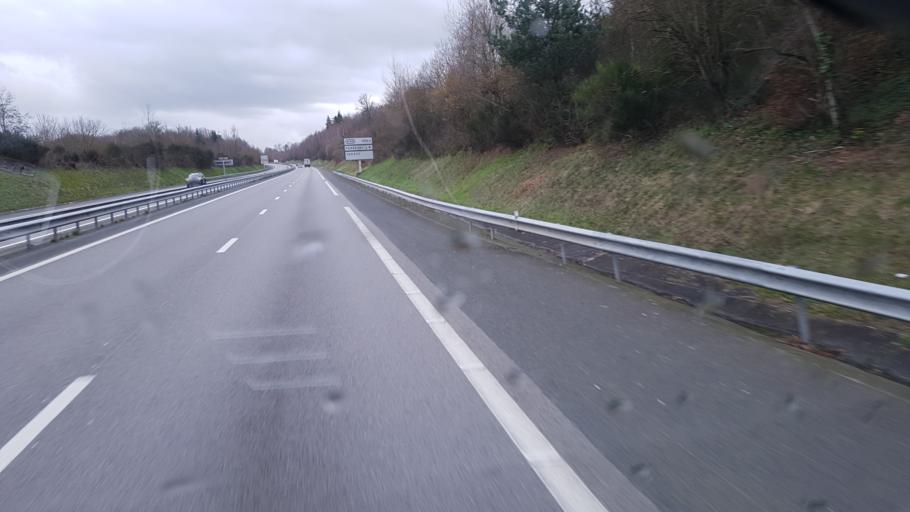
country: FR
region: Limousin
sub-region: Departement de la Correze
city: Vigeois
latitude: 45.3322
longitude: 1.5725
